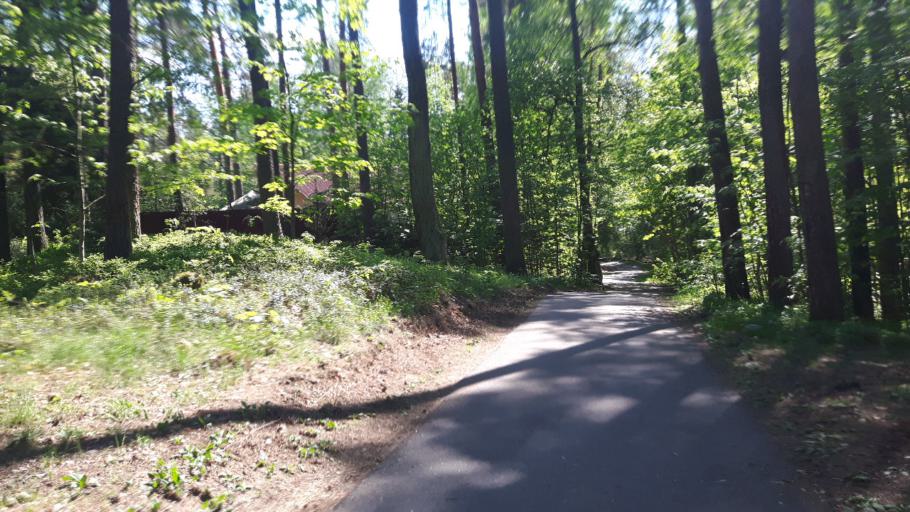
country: RU
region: St.-Petersburg
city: Komarovo
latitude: 60.1660
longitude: 29.8344
